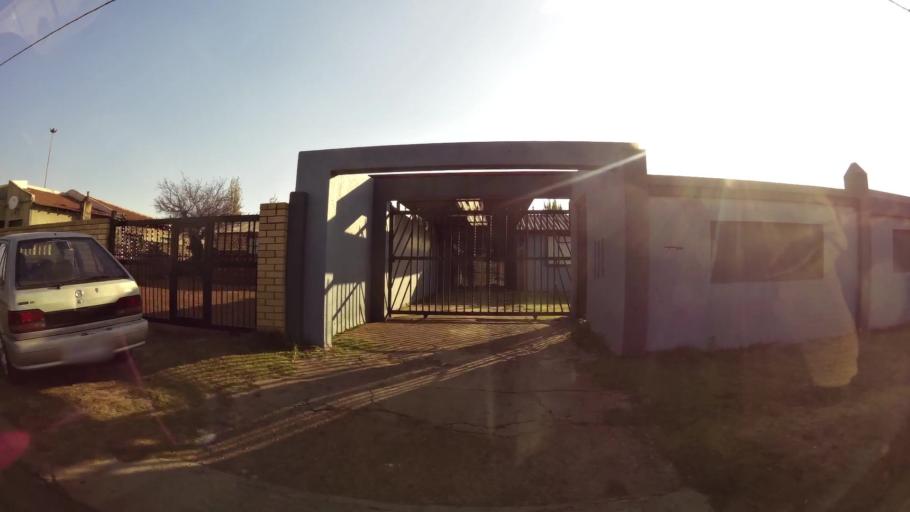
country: ZA
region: Gauteng
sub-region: City of Johannesburg Metropolitan Municipality
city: Soweto
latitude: -26.2659
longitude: 27.8758
